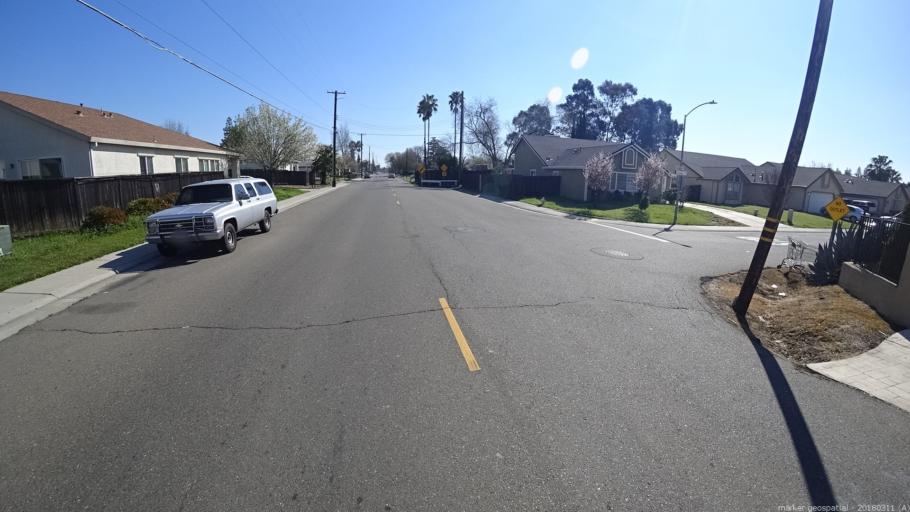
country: US
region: California
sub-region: Sacramento County
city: Florin
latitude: 38.4653
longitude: -121.4008
